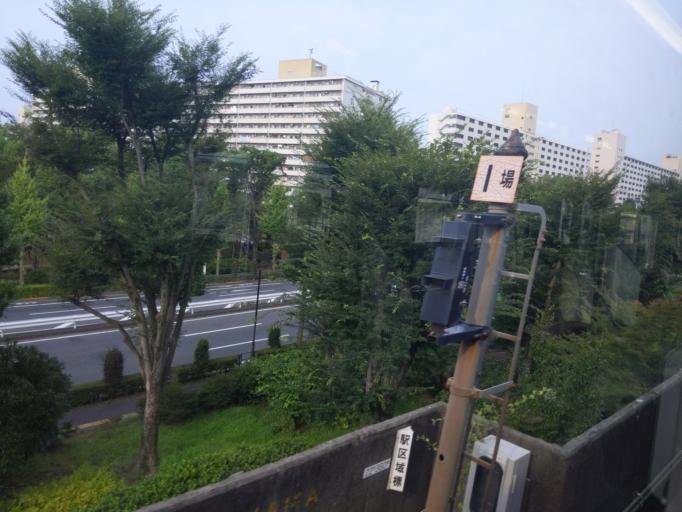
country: JP
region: Saitama
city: Shimotoda
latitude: 35.7881
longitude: 139.6651
